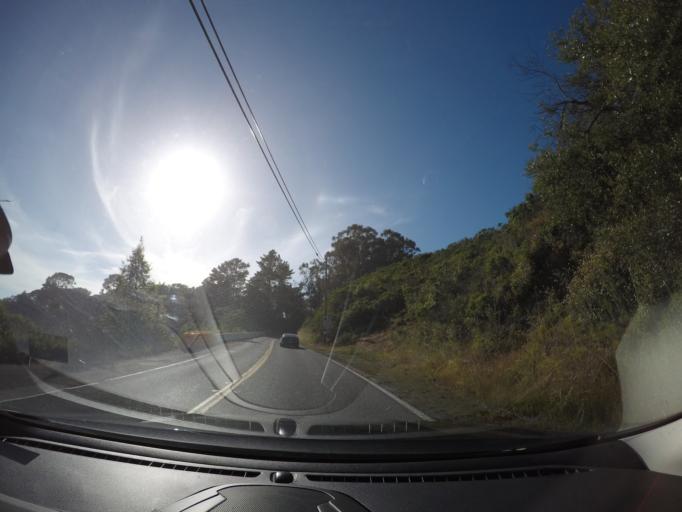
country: US
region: California
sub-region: Monterey County
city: Carmel Valley Village
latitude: 36.2268
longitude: -121.7630
